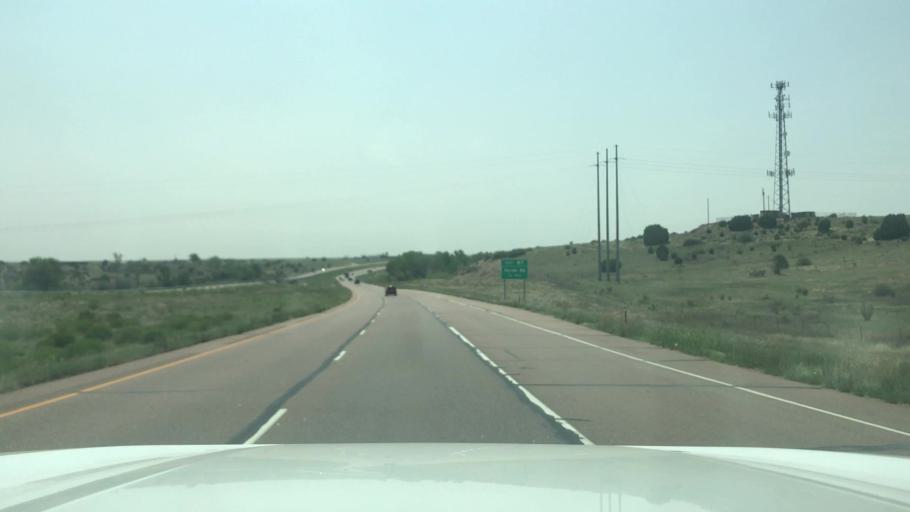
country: US
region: Colorado
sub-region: Pueblo County
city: Pueblo
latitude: 38.1253
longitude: -104.6710
